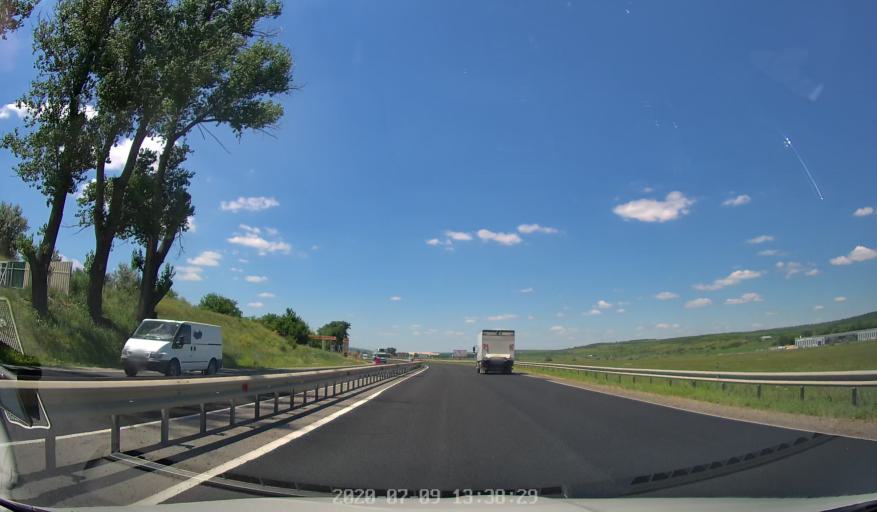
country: MD
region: Chisinau
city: Cricova
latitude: 47.1665
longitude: 28.8194
